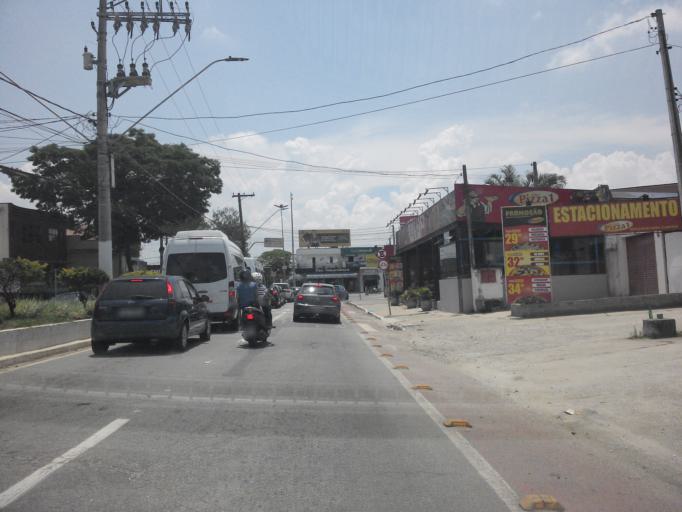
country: BR
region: Sao Paulo
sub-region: Taubate
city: Taubate
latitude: -23.0394
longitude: -45.5846
